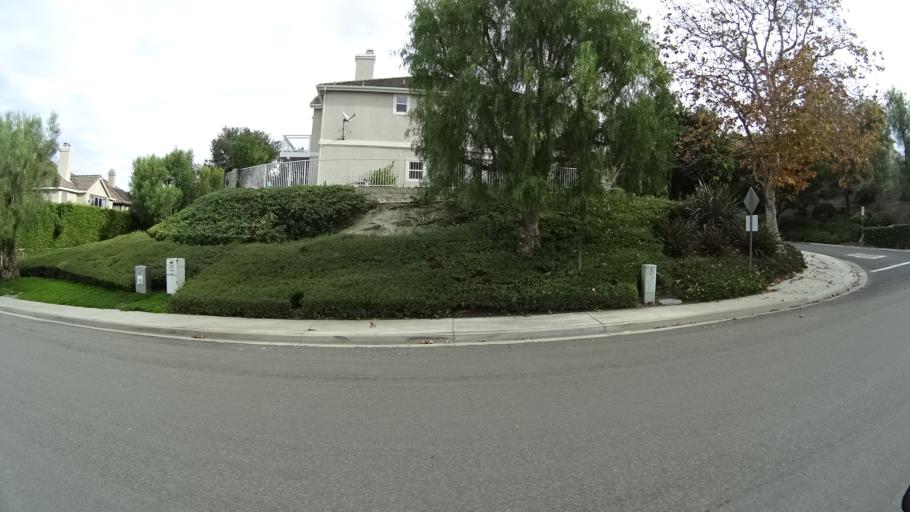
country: US
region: California
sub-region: Orange County
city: Aliso Viejo
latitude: 33.5801
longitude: -117.7445
